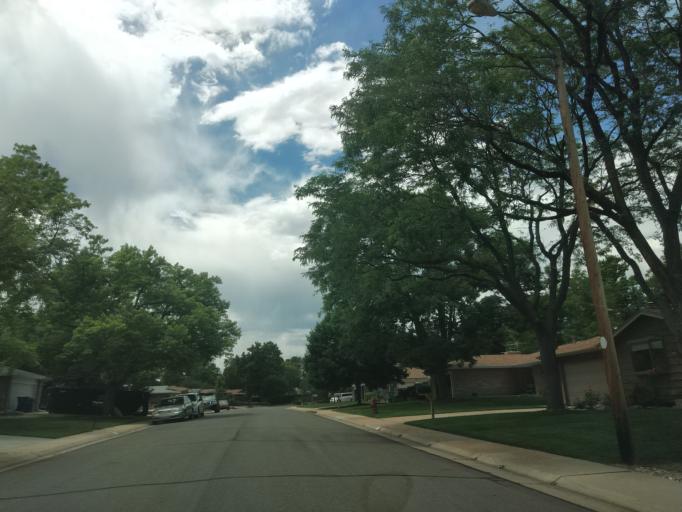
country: US
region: Colorado
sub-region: Jefferson County
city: Lakewood
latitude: 39.6796
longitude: -105.0968
